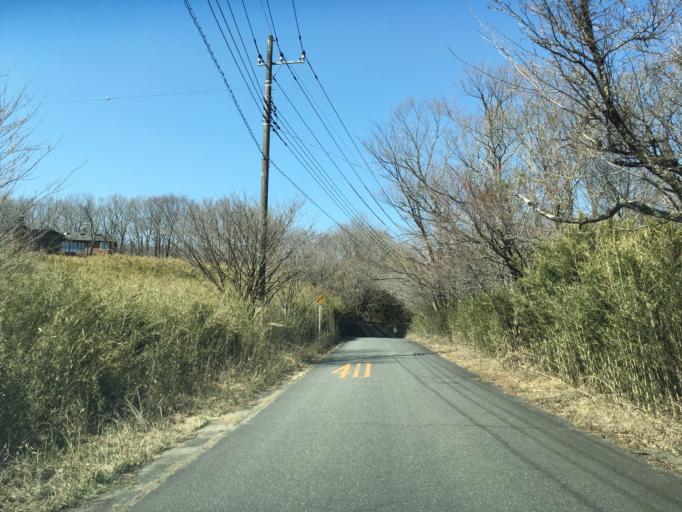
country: JP
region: Tochigi
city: Kuroiso
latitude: 37.0691
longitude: 140.0030
